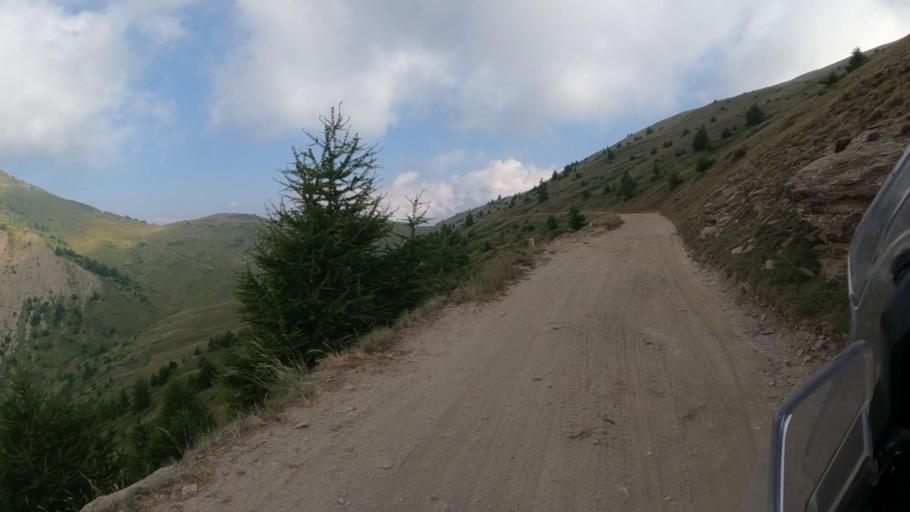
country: IT
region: Piedmont
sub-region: Provincia di Torino
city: Pragelato-Rua
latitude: 45.0336
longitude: 6.9204
